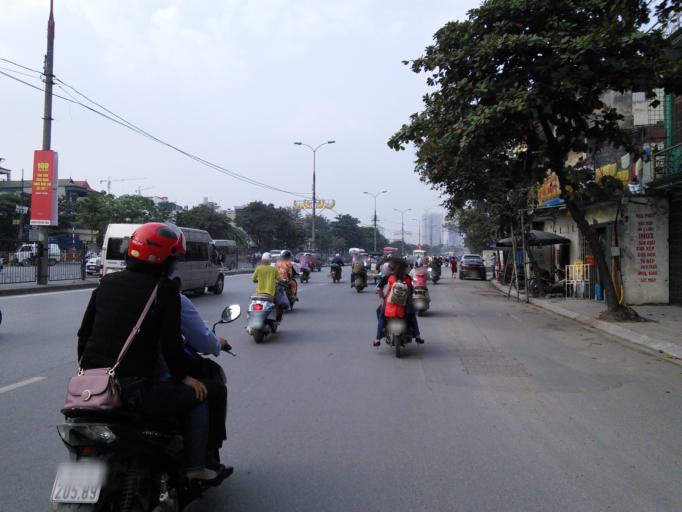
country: VN
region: Ha Noi
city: Van Dien
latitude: 20.9720
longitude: 105.8409
